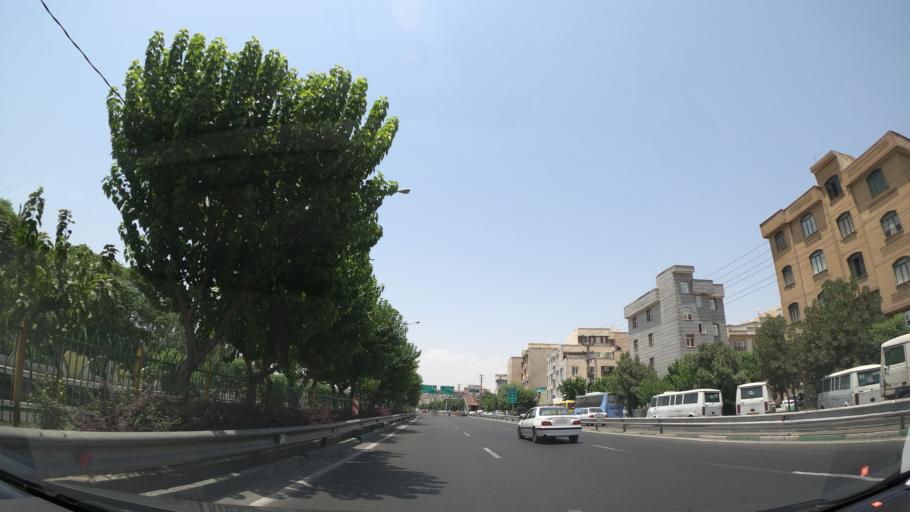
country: IR
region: Tehran
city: Tehran
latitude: 35.6480
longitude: 51.3908
